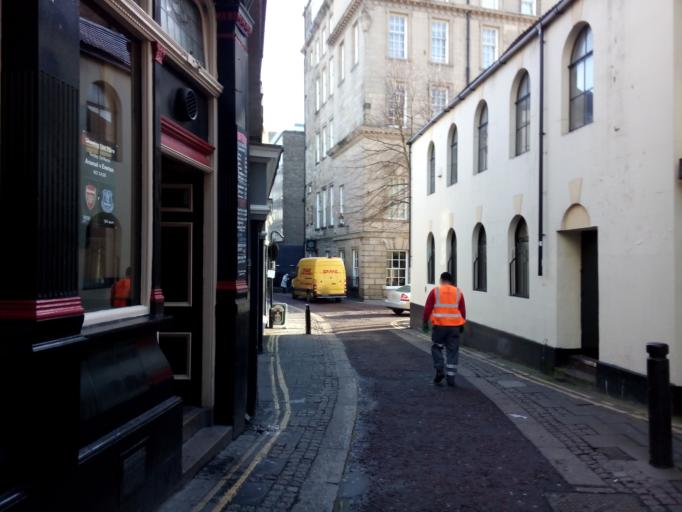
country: GB
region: England
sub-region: Newcastle upon Tyne
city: Newcastle upon Tyne
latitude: 54.9698
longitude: -1.6190
